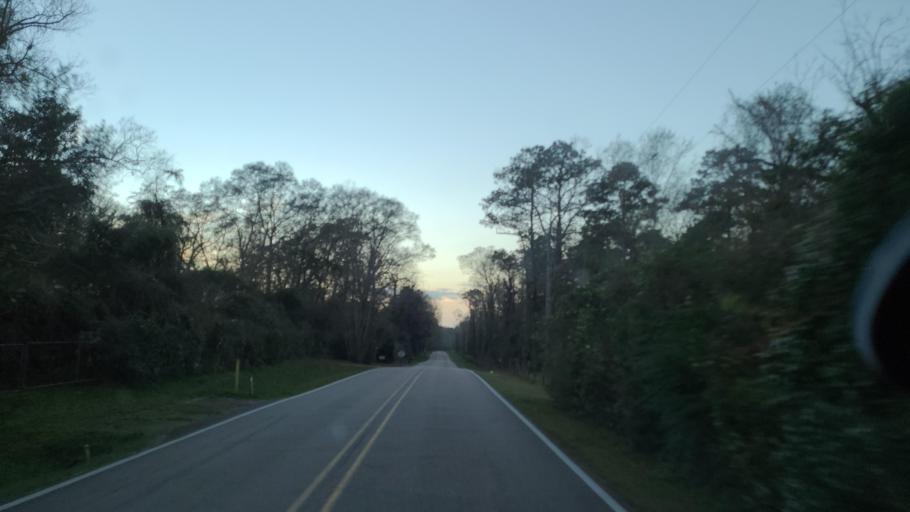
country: US
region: Mississippi
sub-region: Forrest County
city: Hattiesburg
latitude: 31.1677
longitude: -89.2260
